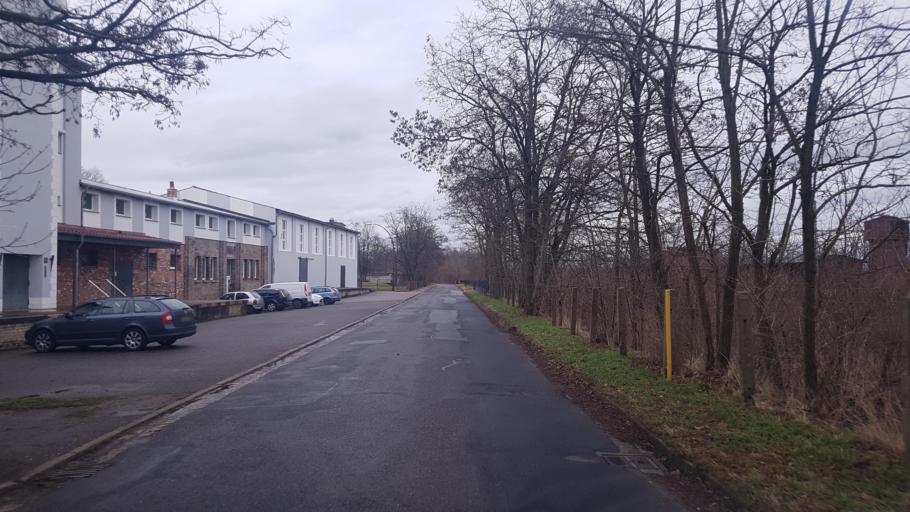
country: DE
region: Brandenburg
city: Elsterwerda
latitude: 51.4729
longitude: 13.5151
